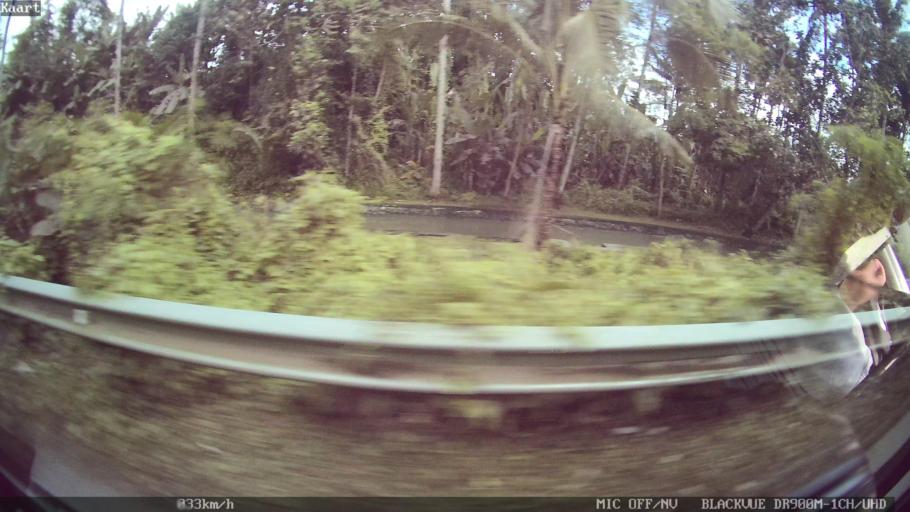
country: ID
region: Bali
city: Banjar Parekan
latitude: -8.5703
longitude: 115.2029
